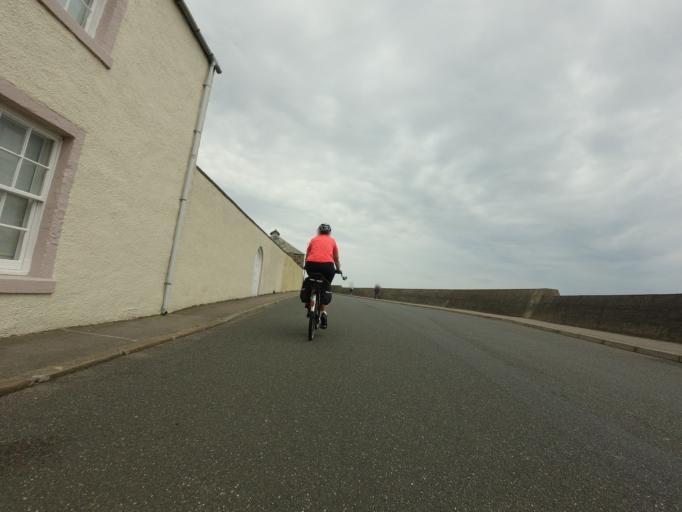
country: GB
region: Scotland
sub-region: Aberdeenshire
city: Banff
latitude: 57.6668
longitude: -2.5207
